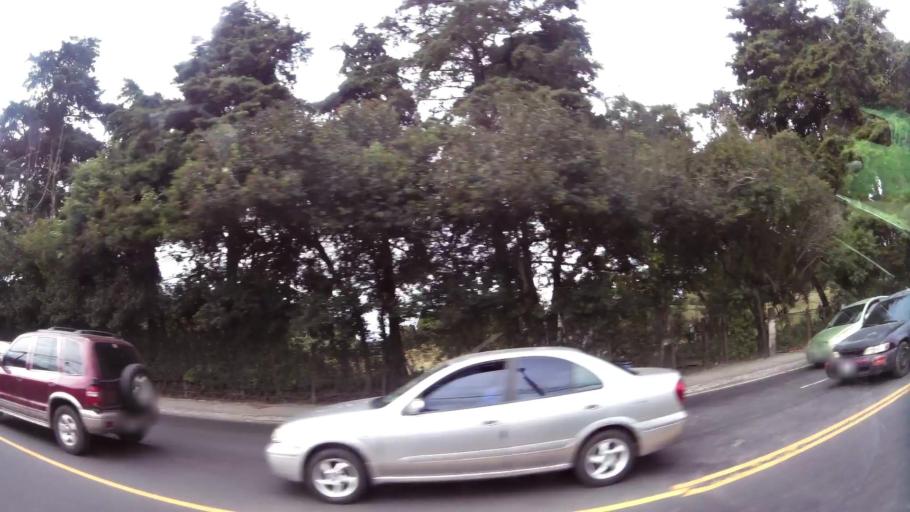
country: GT
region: Guatemala
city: Guatemala City
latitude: 14.6325
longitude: -90.5475
